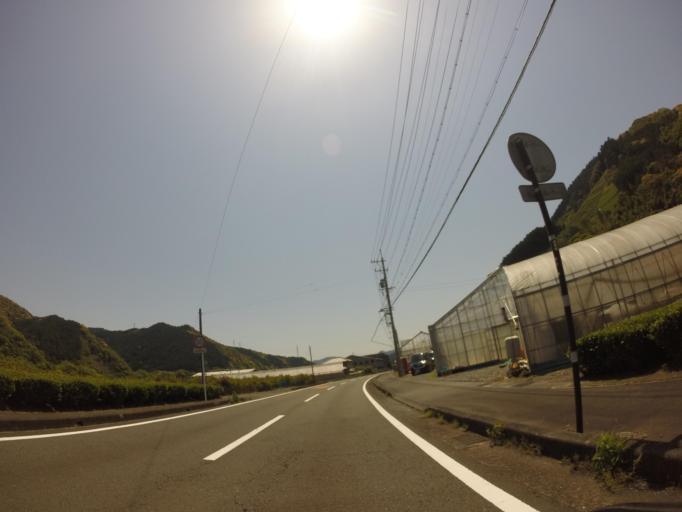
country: JP
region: Shizuoka
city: Shizuoka-shi
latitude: 35.0039
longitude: 138.2812
